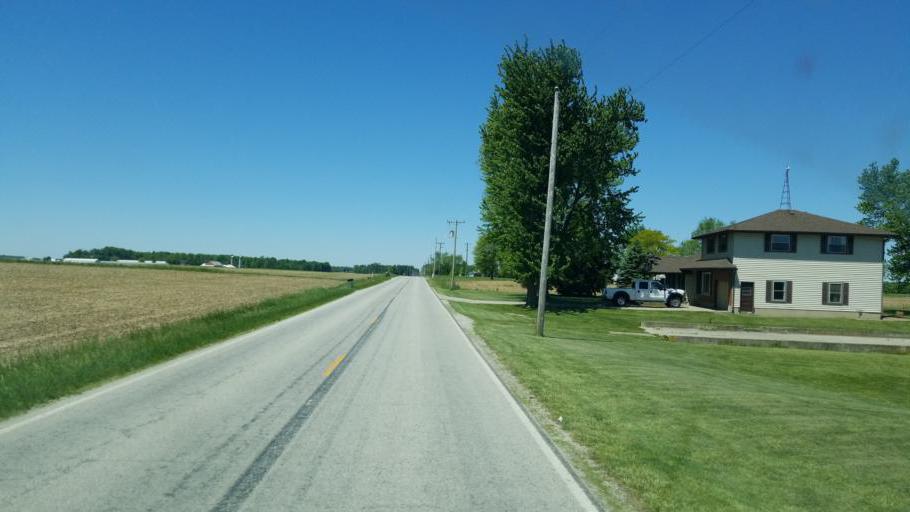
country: US
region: Ohio
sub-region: Shelby County
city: Fort Loramie
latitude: 40.3570
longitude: -84.3110
